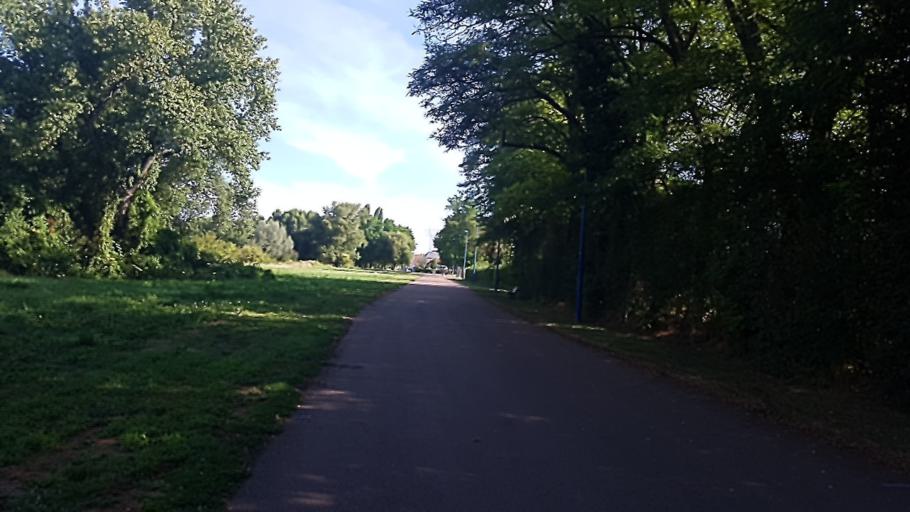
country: FR
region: Bourgogne
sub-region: Departement de la Nievre
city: Imphy
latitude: 46.9232
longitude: 3.2594
